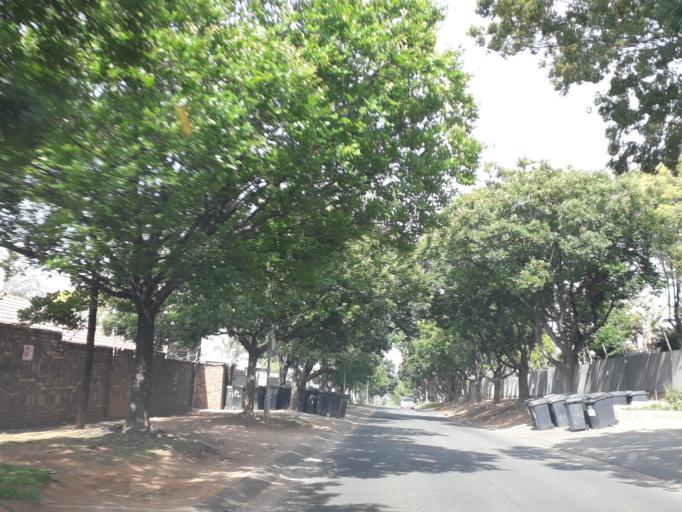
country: ZA
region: Gauteng
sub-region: City of Johannesburg Metropolitan Municipality
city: Roodepoort
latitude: -26.0718
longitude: 27.9594
